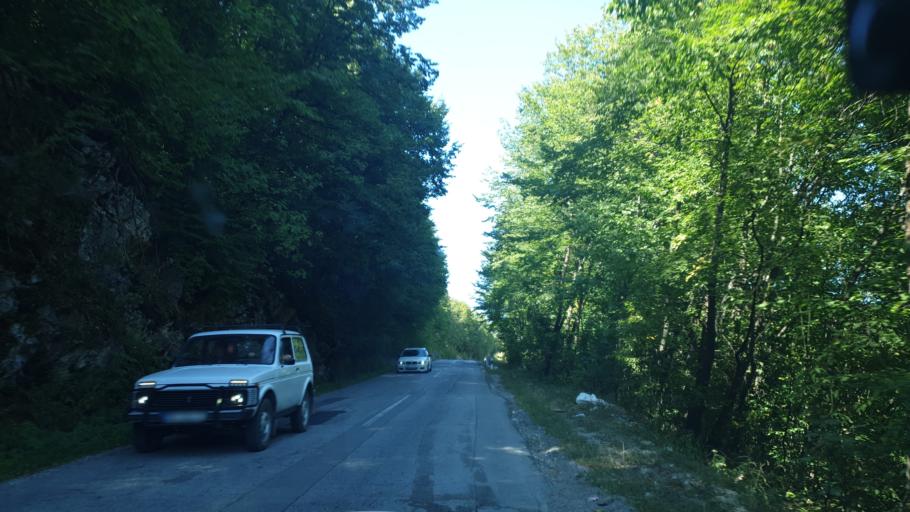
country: RS
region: Central Serbia
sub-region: Kolubarski Okrug
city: Mionica
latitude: 44.1499
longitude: 20.0212
